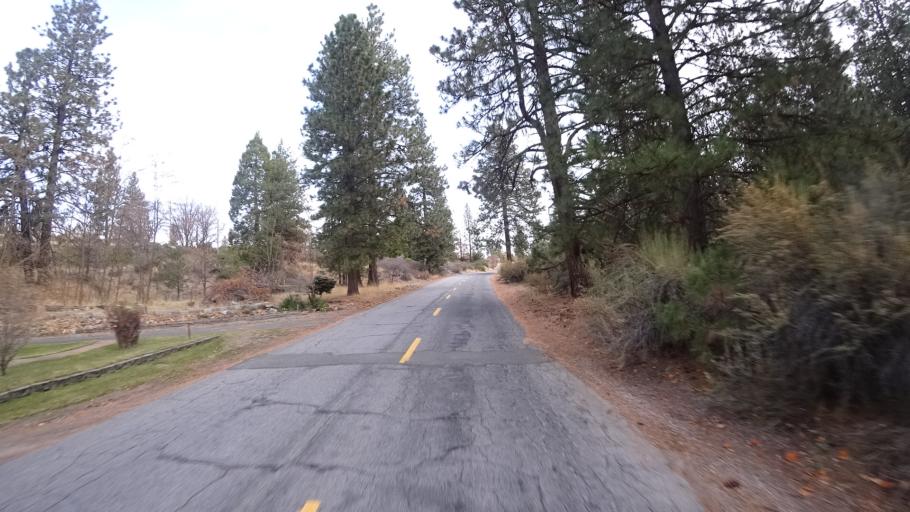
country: US
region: California
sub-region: Siskiyou County
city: Weed
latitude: 41.4420
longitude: -122.3753
